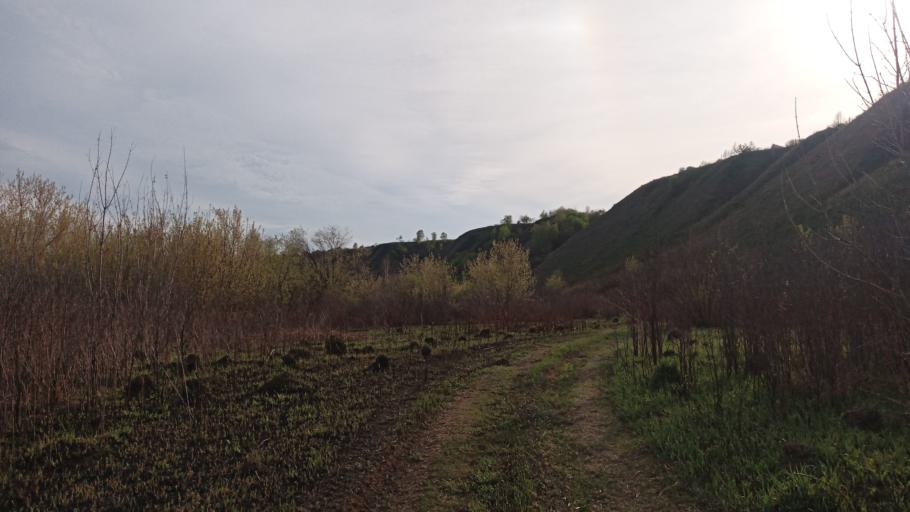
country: RU
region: Altai Krai
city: Yuzhnyy
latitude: 53.2230
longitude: 83.7271
